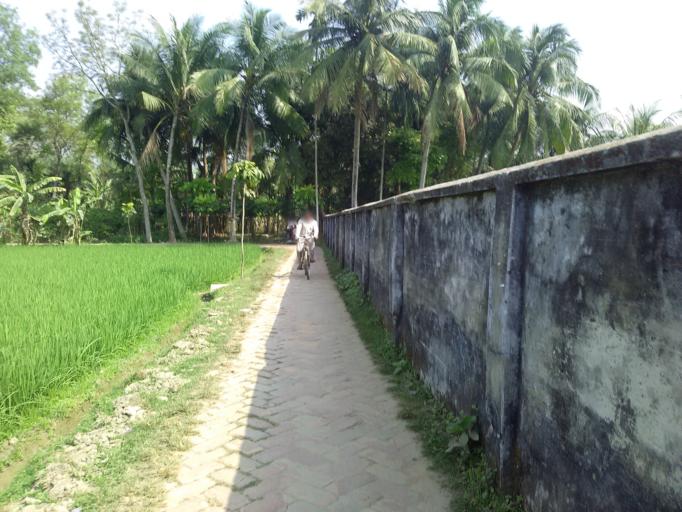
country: BD
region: Khulna
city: Khulna
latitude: 22.8926
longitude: 89.5348
